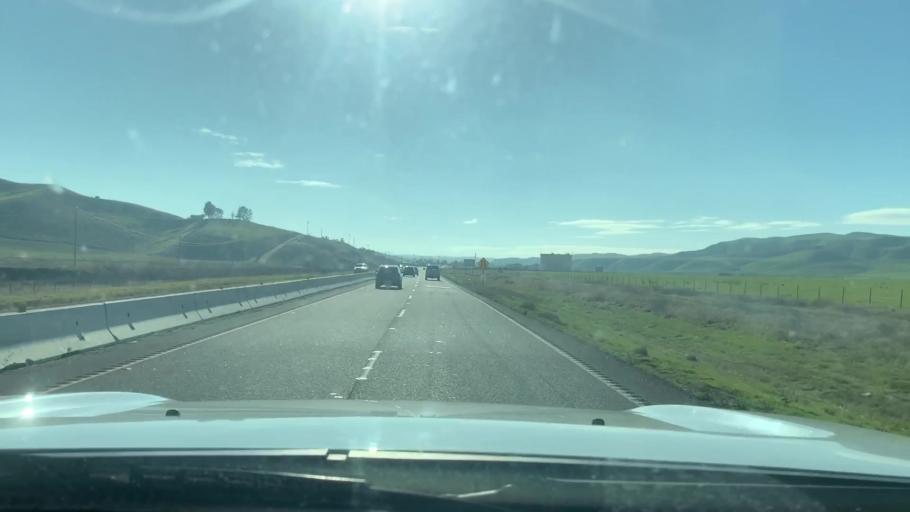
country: US
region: California
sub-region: San Luis Obispo County
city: Shandon
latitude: 35.6944
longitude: -120.3299
